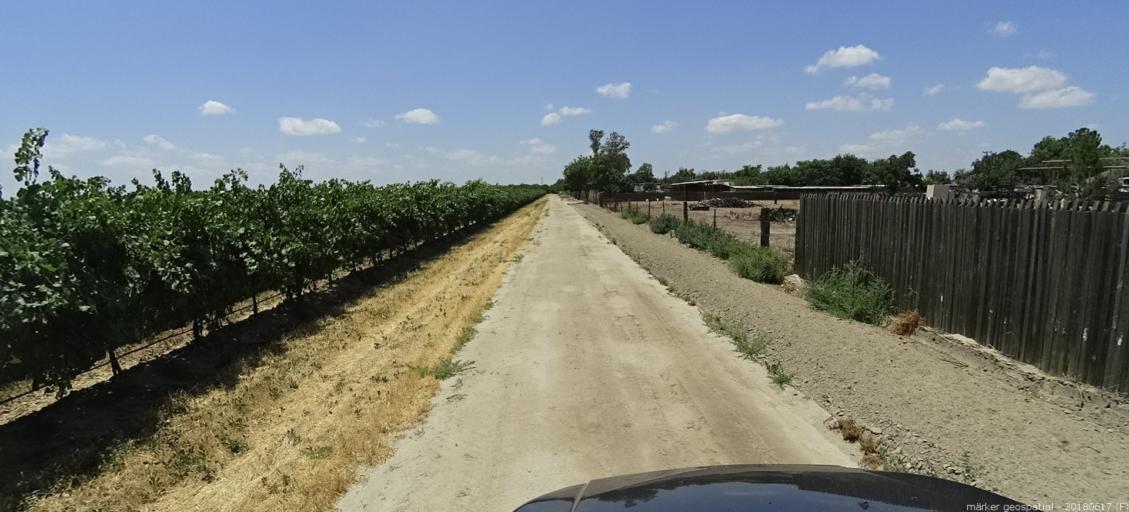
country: US
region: California
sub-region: Madera County
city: Parkwood
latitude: 36.8356
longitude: -120.1720
